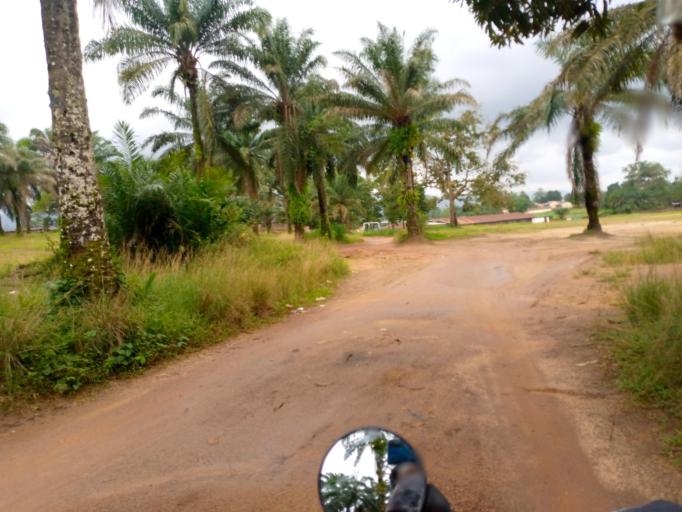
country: SL
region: Eastern Province
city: Kenema
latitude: 7.8649
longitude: -11.1849
